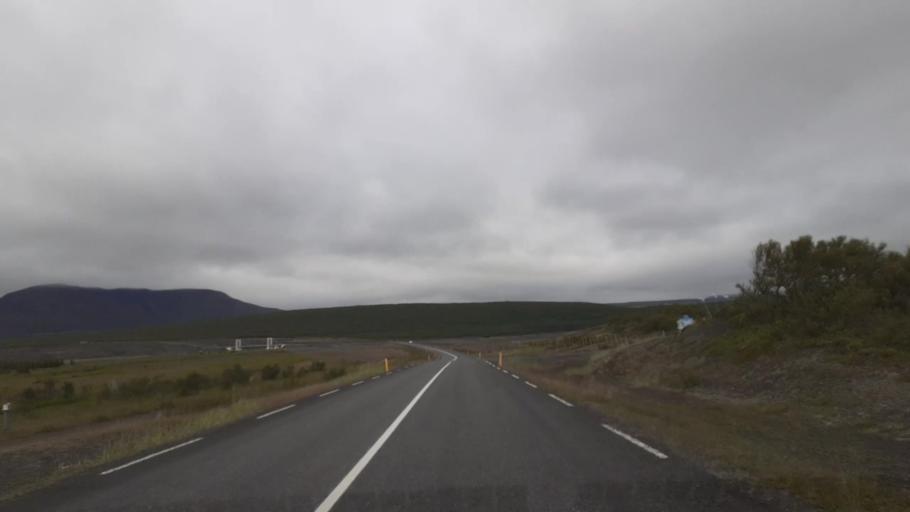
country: IS
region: Northeast
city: Husavik
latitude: 66.0307
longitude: -16.4681
